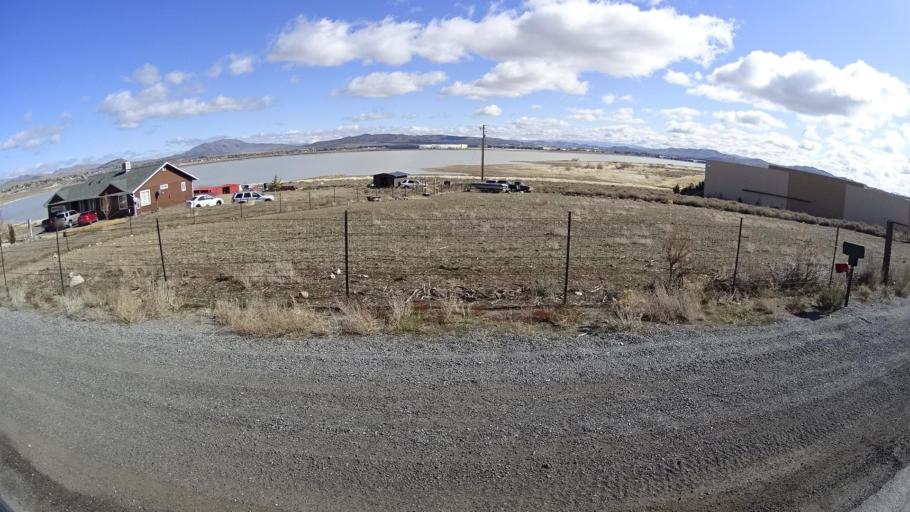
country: US
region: Nevada
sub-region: Washoe County
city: Cold Springs
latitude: 39.6384
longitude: -119.9232
